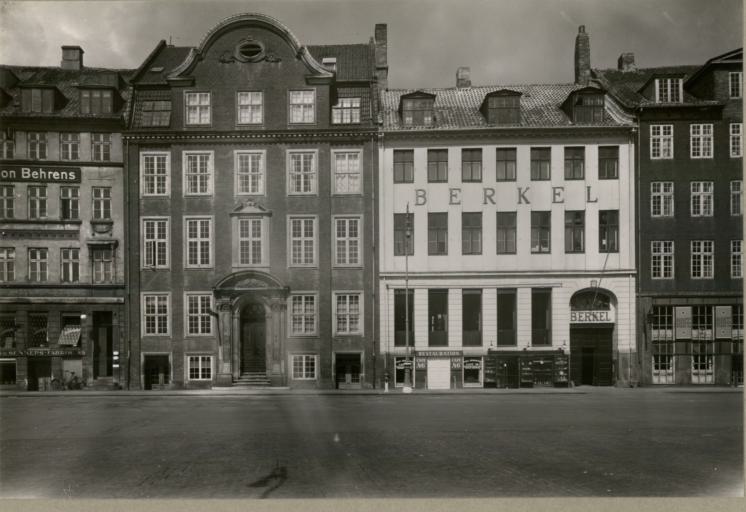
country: DK
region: Capital Region
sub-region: Kobenhavn
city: Copenhagen
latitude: 55.6772
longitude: 12.5779
